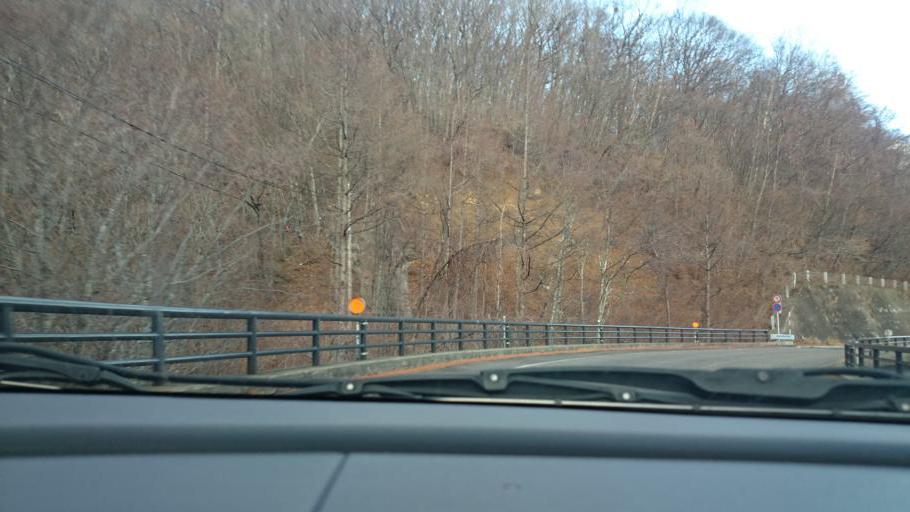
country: JP
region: Tochigi
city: Kuroiso
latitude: 37.1617
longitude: 140.0178
